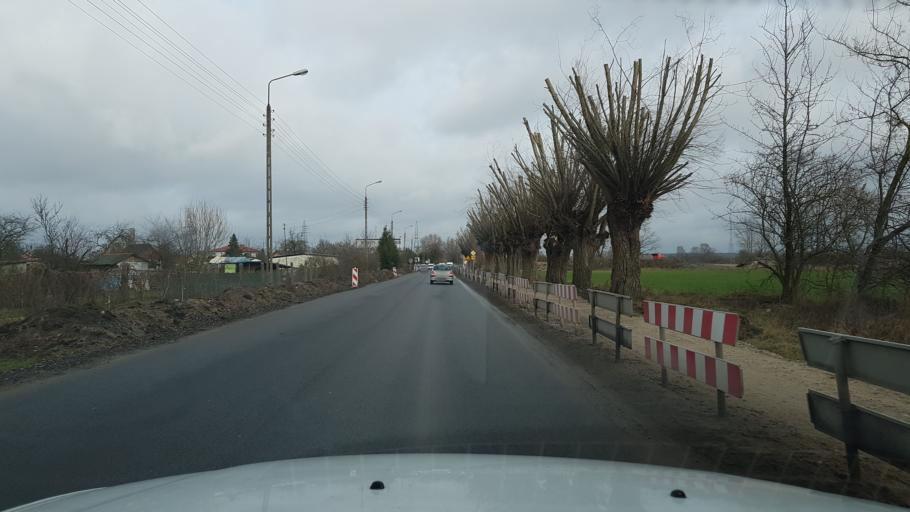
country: PL
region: West Pomeranian Voivodeship
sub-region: Powiat szczecinecki
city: Szczecinek
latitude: 53.7145
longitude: 16.7152
